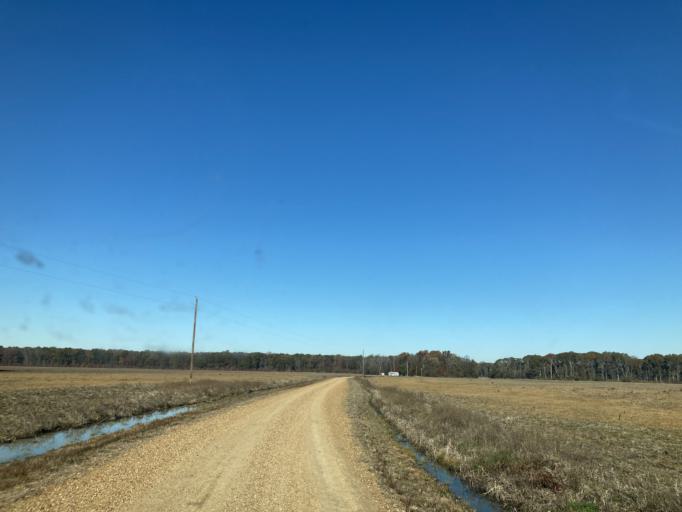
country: US
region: Mississippi
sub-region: Sharkey County
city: Rolling Fork
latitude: 32.9017
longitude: -90.6649
